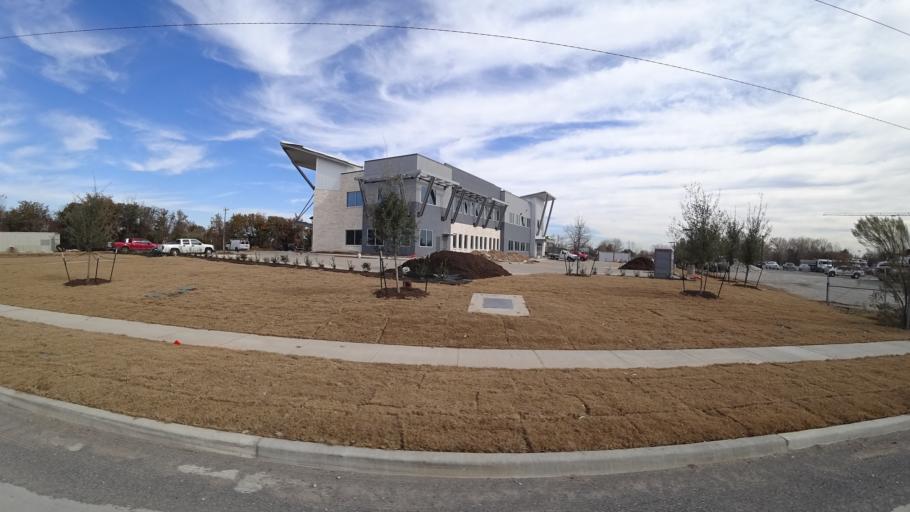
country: US
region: Texas
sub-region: Denton County
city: Lewisville
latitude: 33.0363
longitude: -96.9801
